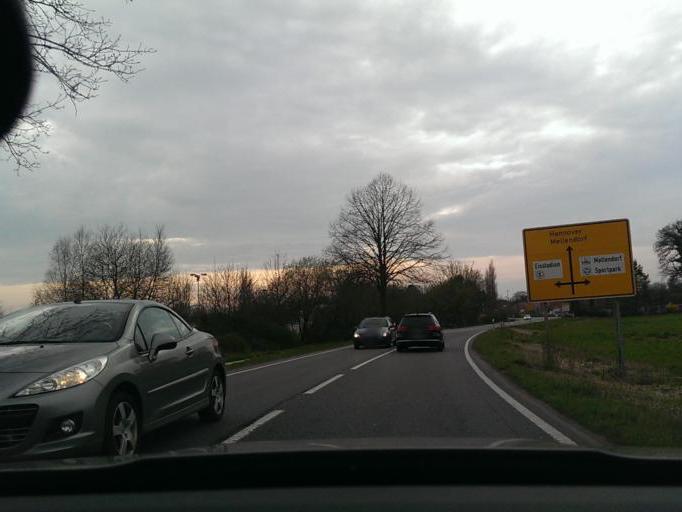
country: DE
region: Lower Saxony
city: Elze
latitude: 52.5473
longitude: 9.7524
